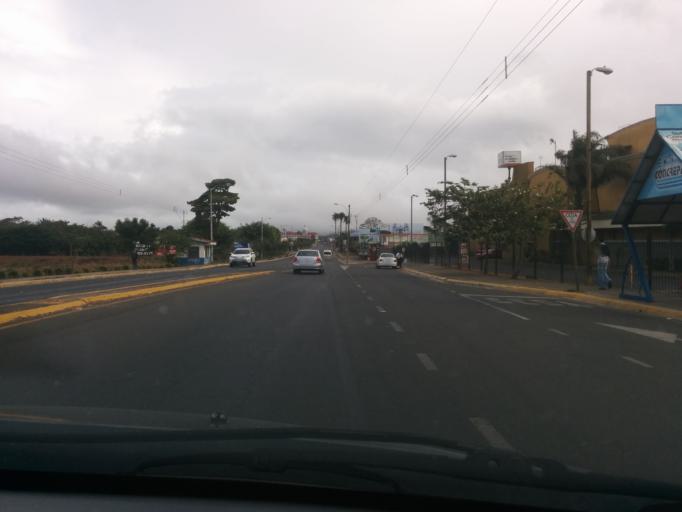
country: CR
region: Alajuela
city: San Ramon
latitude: 10.0774
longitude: -84.4700
